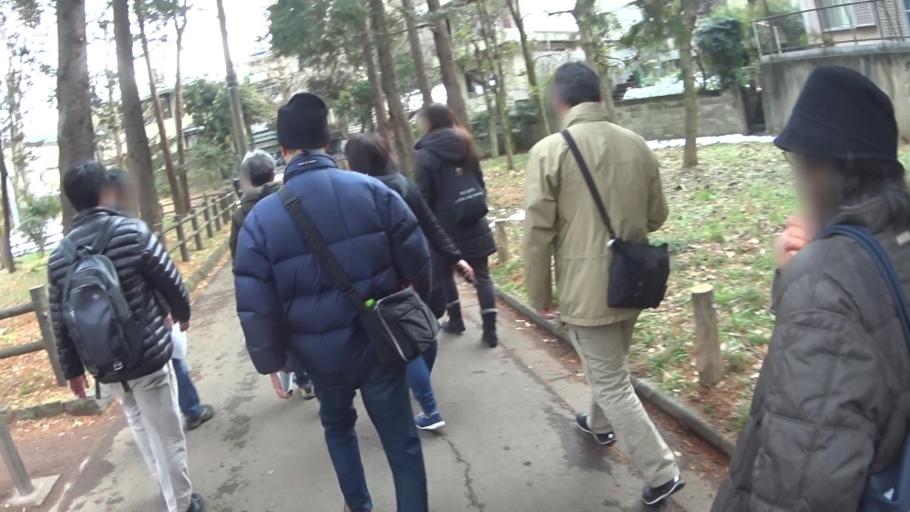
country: JP
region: Tokyo
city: Musashino
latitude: 35.7122
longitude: 139.5915
